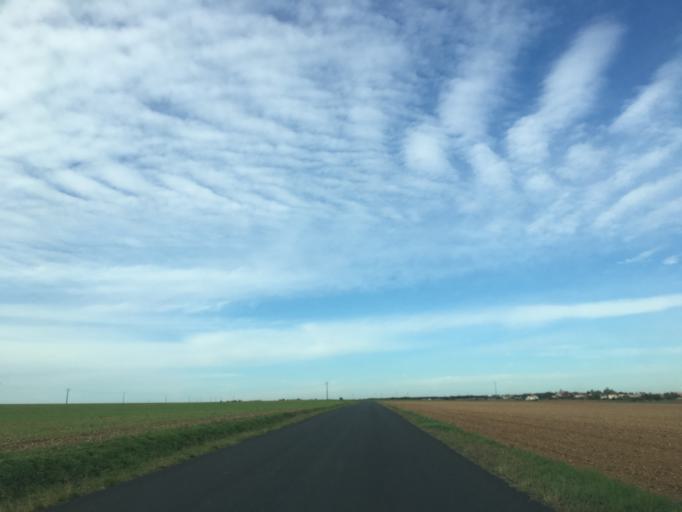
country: FR
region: Poitou-Charentes
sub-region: Departement des Deux-Sevres
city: Beauvoir-sur-Niort
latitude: 46.0698
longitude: -0.4831
